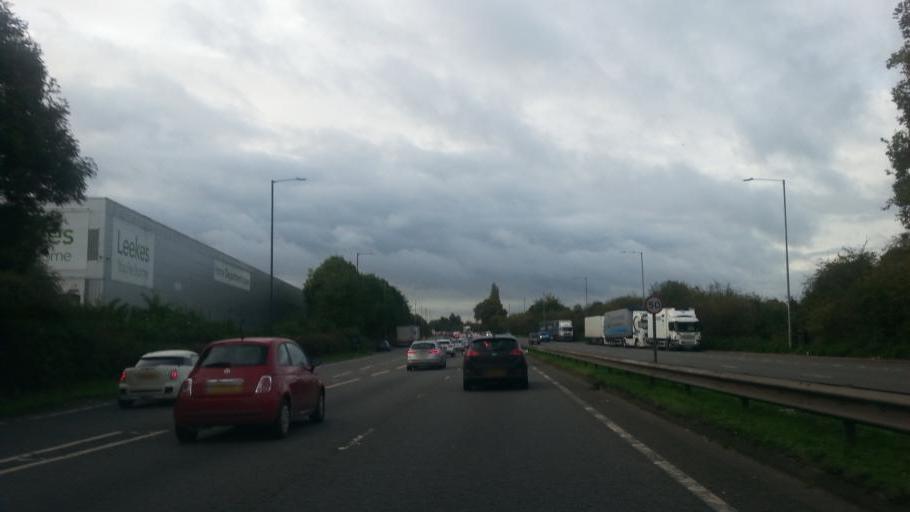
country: GB
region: England
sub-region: Warwickshire
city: Exhall
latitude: 52.4557
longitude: -1.4990
